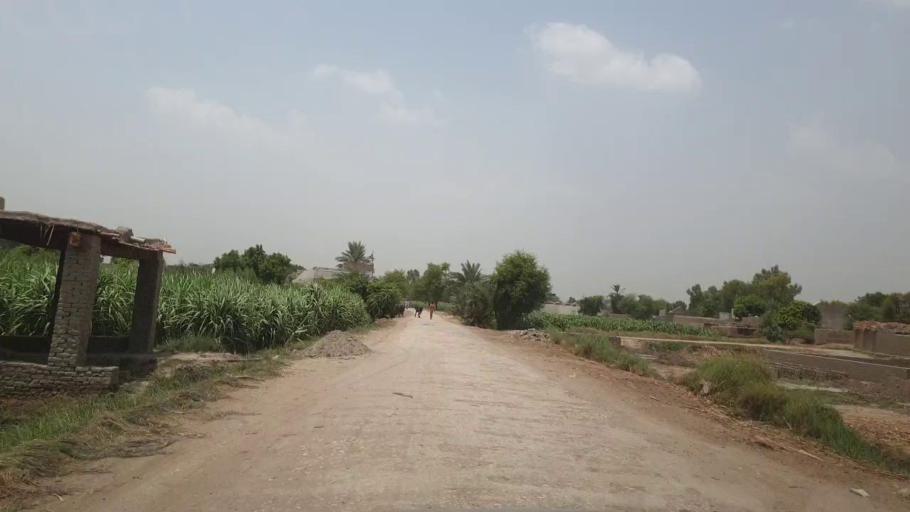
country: PK
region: Sindh
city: Sobhadero
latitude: 27.4388
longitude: 68.3928
